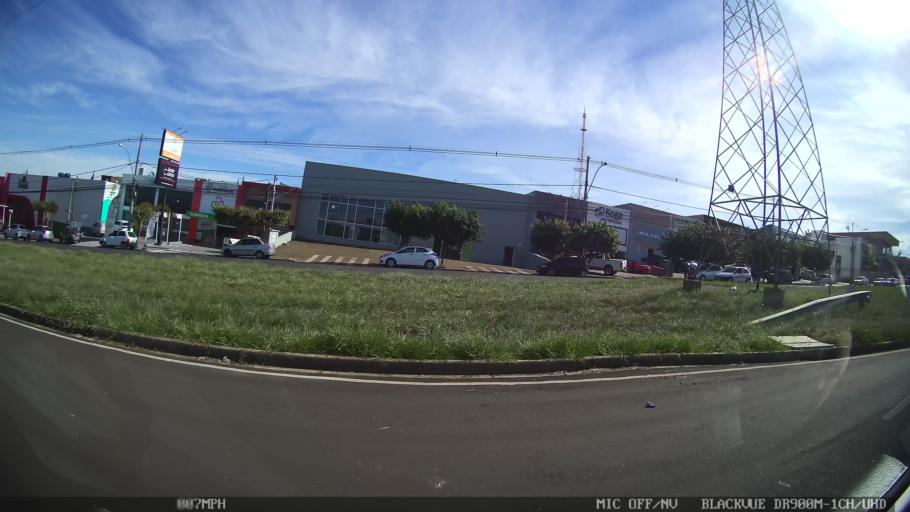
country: BR
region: Sao Paulo
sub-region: Sao Jose Do Rio Preto
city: Sao Jose do Rio Preto
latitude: -20.8032
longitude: -49.3446
